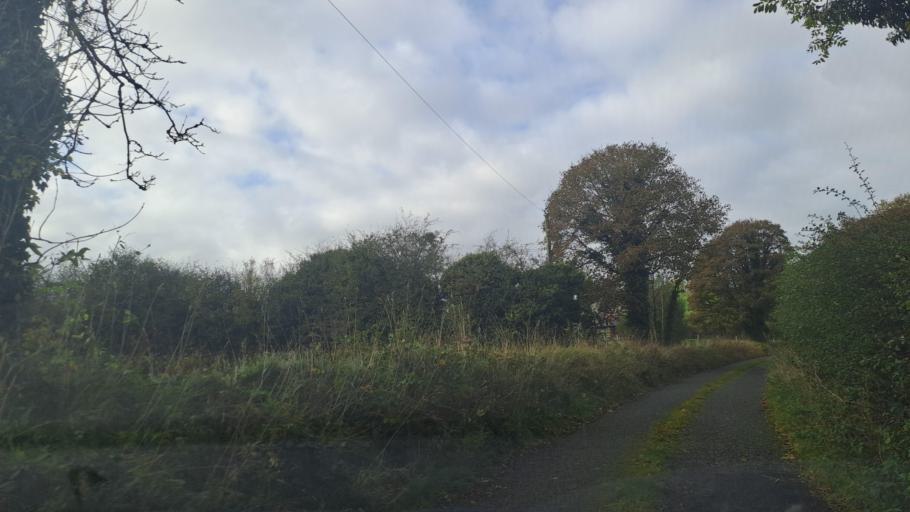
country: IE
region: Ulster
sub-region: An Cabhan
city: Kingscourt
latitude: 53.9999
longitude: -6.8161
